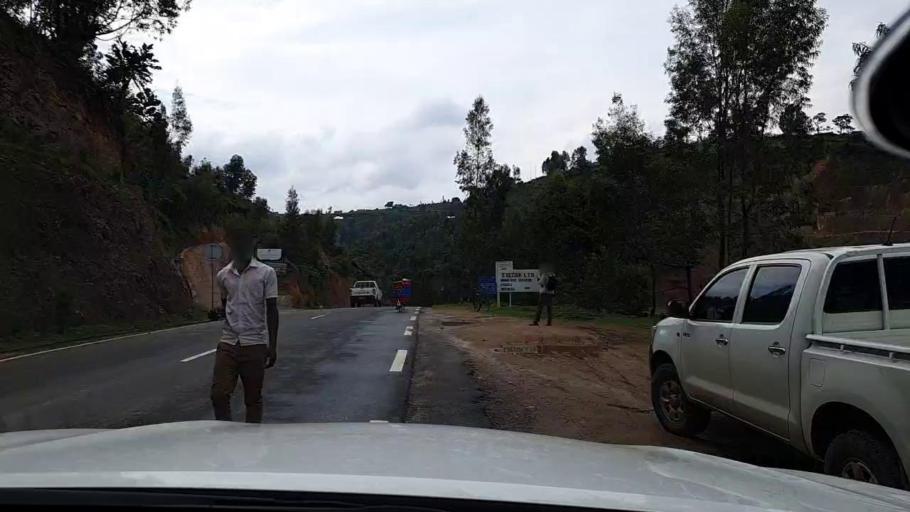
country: RW
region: Western Province
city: Kibuye
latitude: -2.1543
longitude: 29.2985
